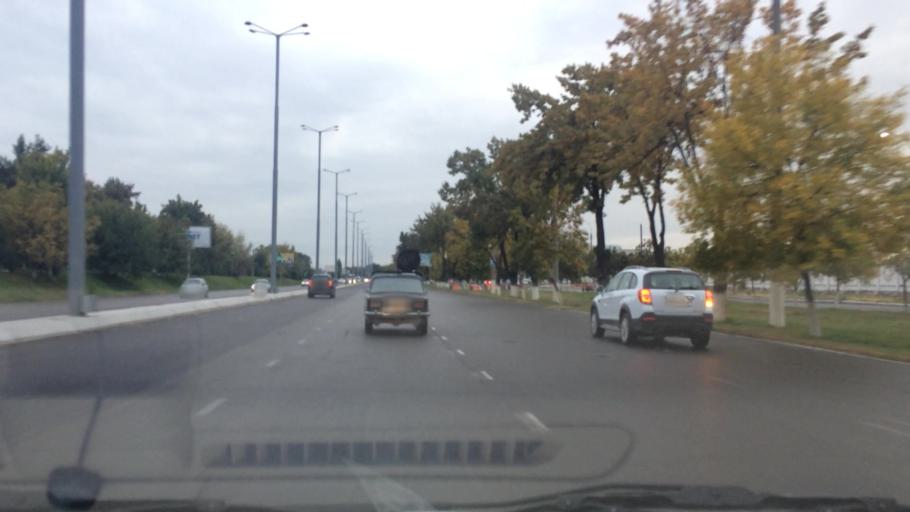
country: UZ
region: Toshkent Shahri
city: Tashkent
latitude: 41.2495
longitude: 69.1816
